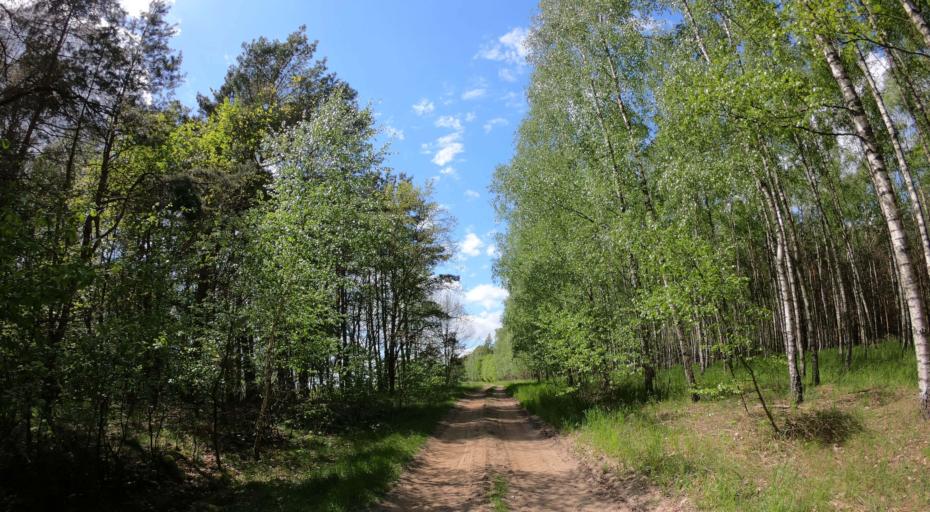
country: PL
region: West Pomeranian Voivodeship
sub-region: Powiat lobeski
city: Lobez
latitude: 53.6056
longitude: 15.6939
